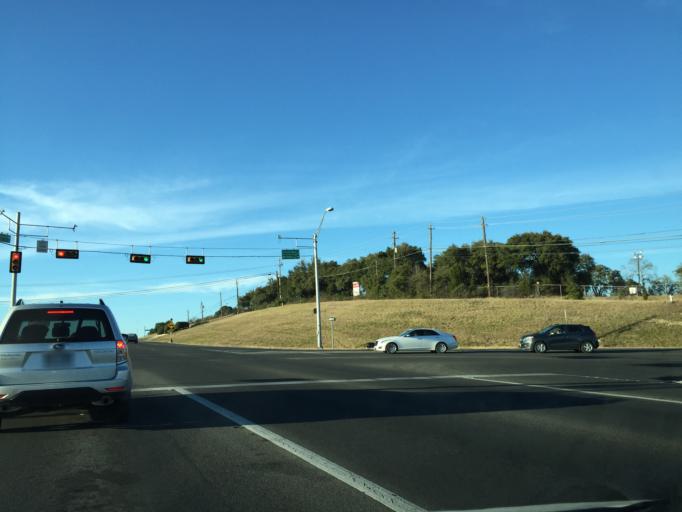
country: US
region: Texas
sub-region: Travis County
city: West Lake Hills
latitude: 30.2773
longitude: -97.8193
